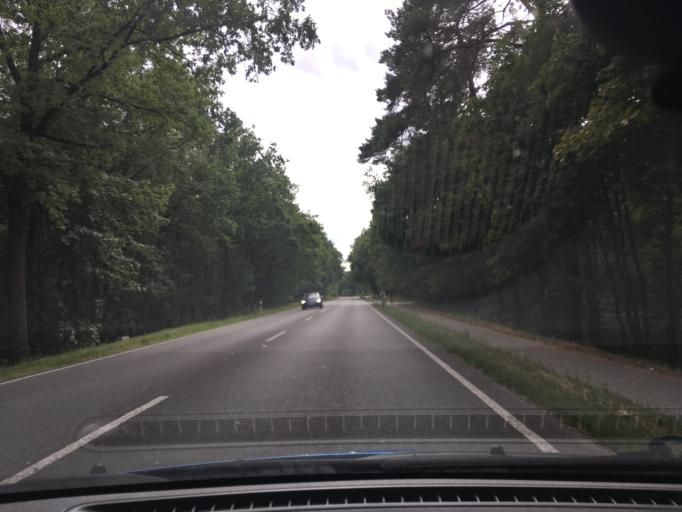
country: DE
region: Lower Saxony
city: Neu Wulmstorf
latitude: 53.4535
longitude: 9.7681
